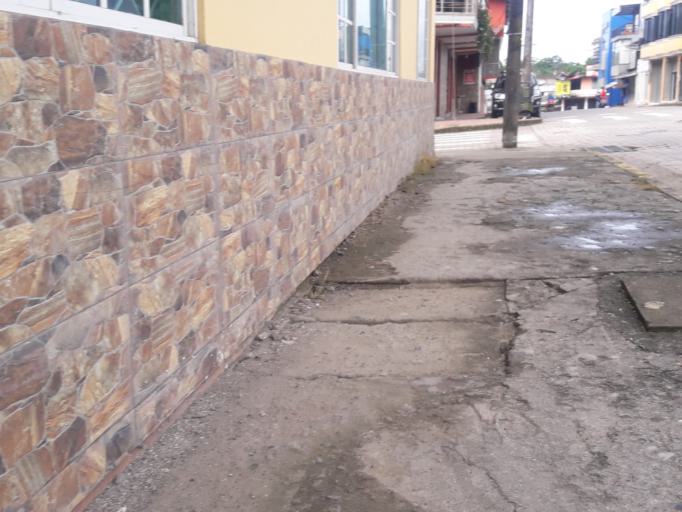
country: EC
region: Napo
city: Tena
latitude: -0.9892
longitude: -77.8149
